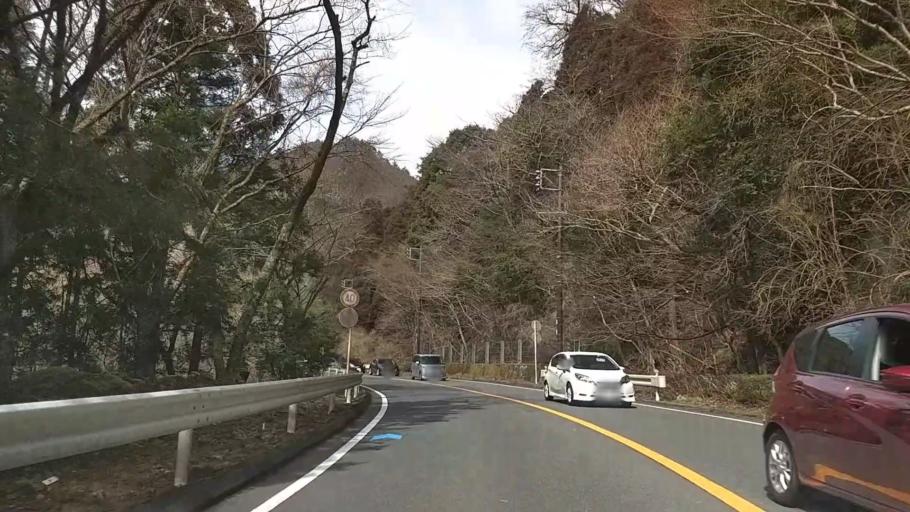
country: JP
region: Shizuoka
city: Shimoda
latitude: 34.8166
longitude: 138.9329
